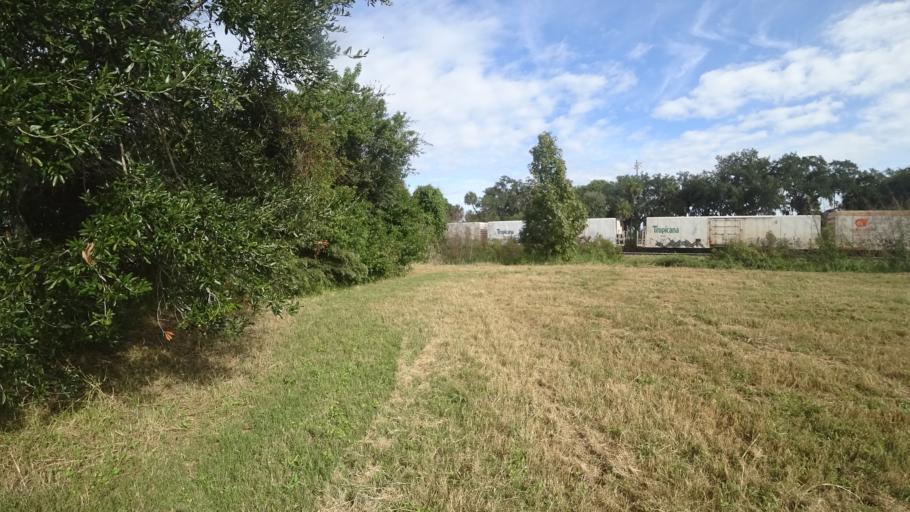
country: US
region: Florida
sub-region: Manatee County
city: West Samoset
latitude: 27.4843
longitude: -82.5605
